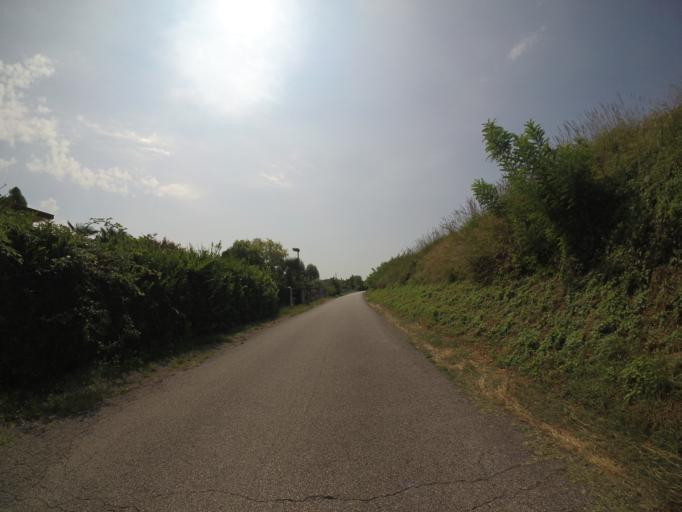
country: IT
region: Friuli Venezia Giulia
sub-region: Provincia di Udine
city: Pertegada
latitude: 45.6975
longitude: 13.0545
